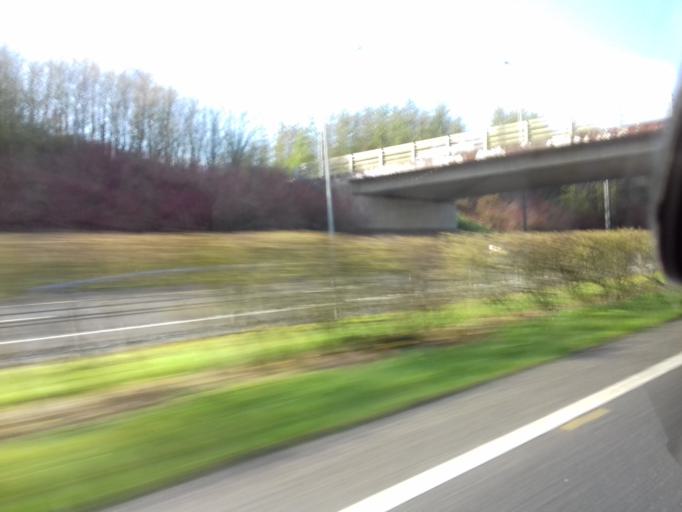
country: IE
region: Leinster
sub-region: Laois
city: Portlaoise
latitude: 53.0496
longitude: -7.2395
